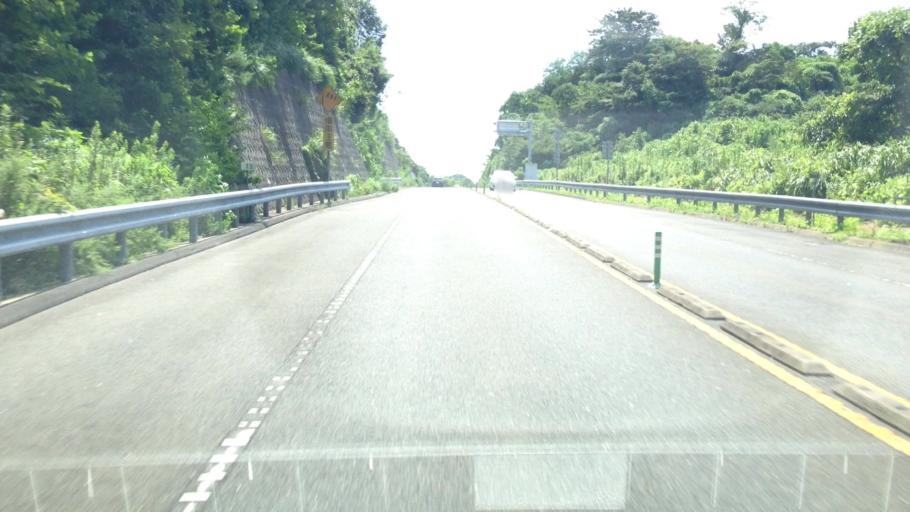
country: JP
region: Kanagawa
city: Yokosuka
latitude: 35.2369
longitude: 139.6516
